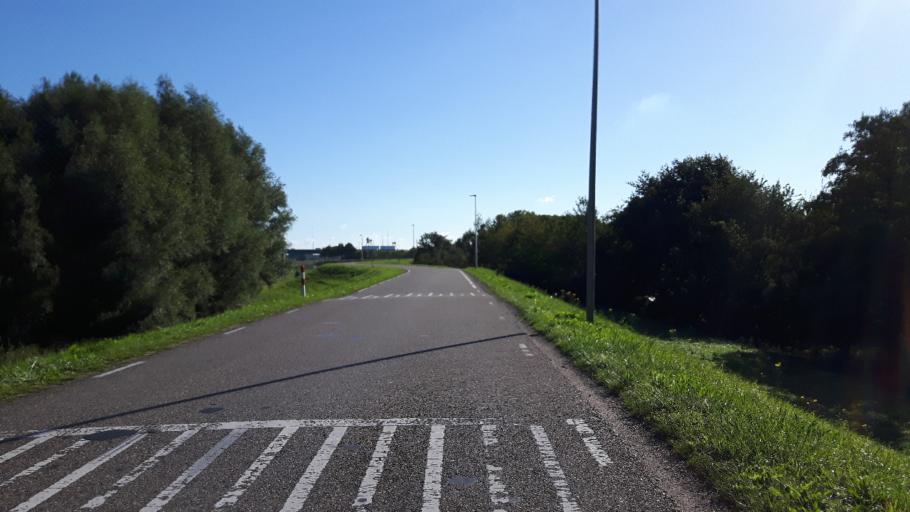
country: NL
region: Utrecht
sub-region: Gemeente Vianen
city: Vianen
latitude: 51.9975
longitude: 5.1048
